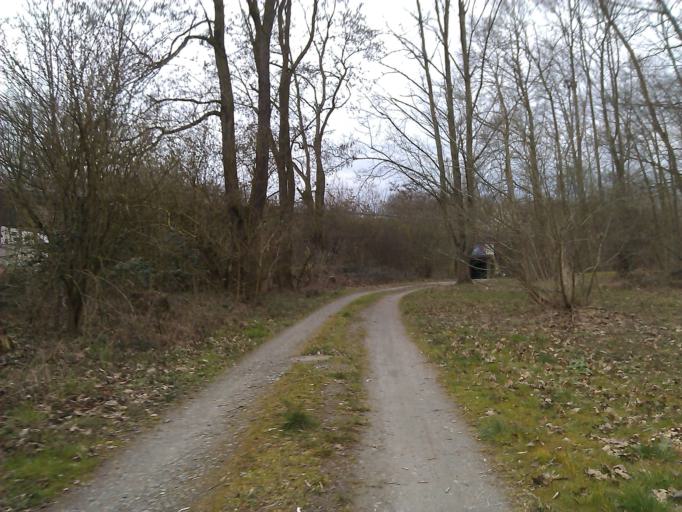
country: DE
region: Hesse
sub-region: Regierungsbezirk Darmstadt
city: Russelsheim
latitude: 49.9614
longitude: 8.4154
